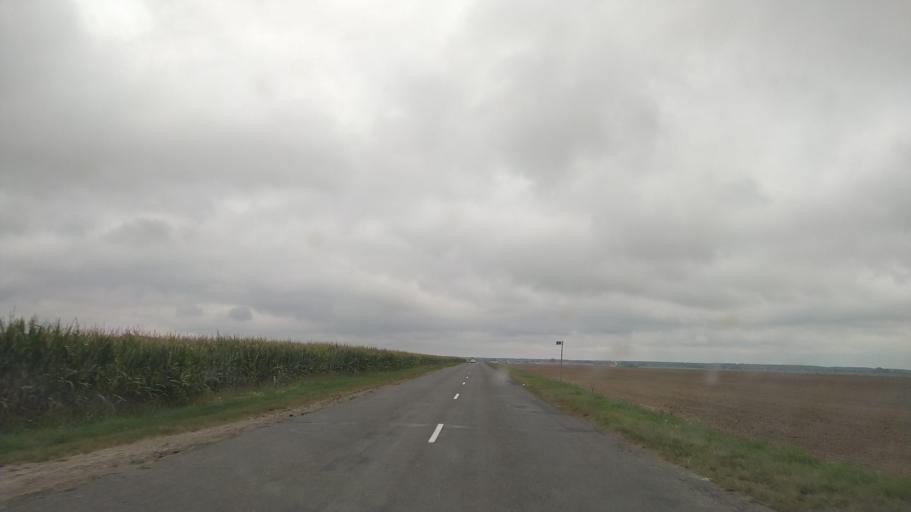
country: BY
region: Brest
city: Byaroza
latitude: 52.5660
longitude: 24.8998
